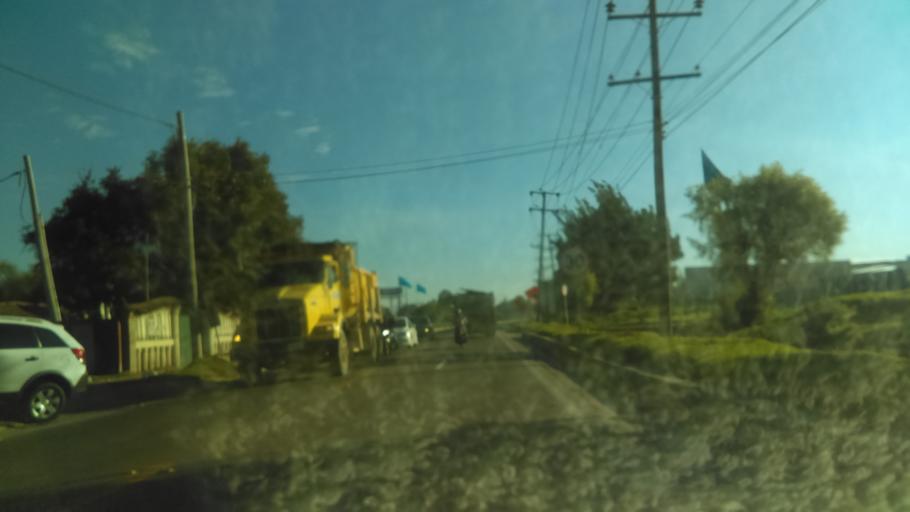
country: CO
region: Cundinamarca
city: Mosquera
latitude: 4.7000
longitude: -74.2378
